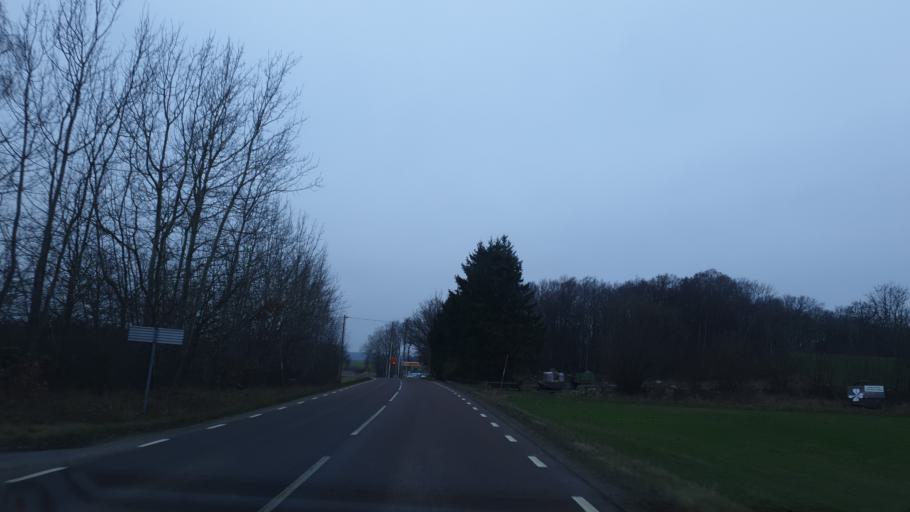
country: SE
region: Blekinge
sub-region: Karlskrona Kommun
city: Jaemjoe
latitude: 56.1586
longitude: 15.7645
